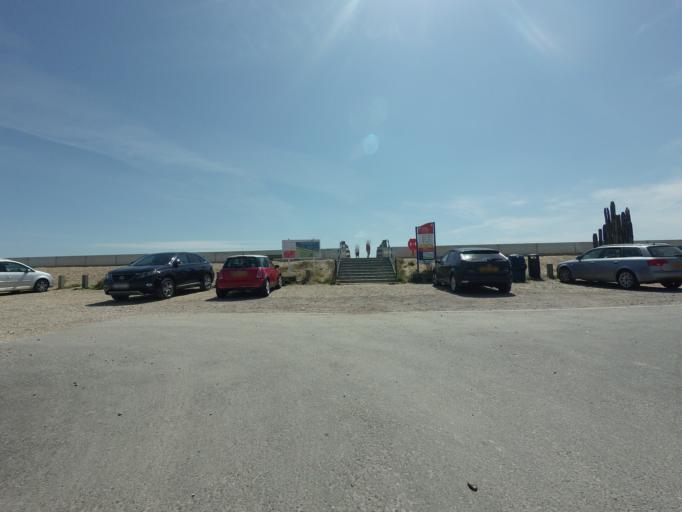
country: GB
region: England
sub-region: East Sussex
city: Rye
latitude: 50.9298
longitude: 0.8171
